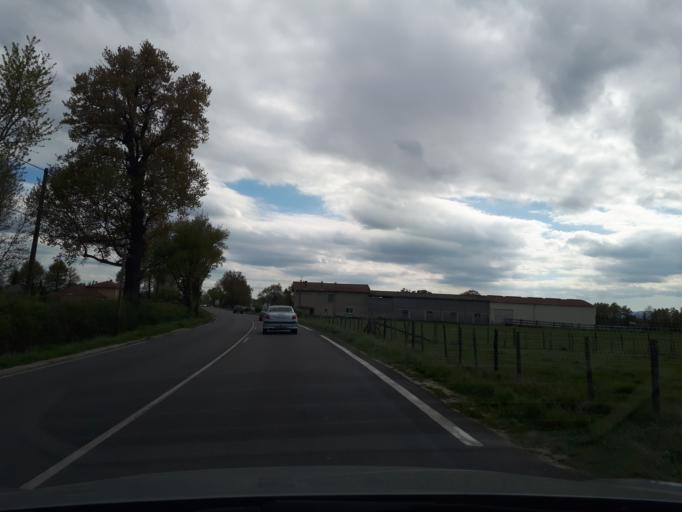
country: FR
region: Rhone-Alpes
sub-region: Departement de la Loire
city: Chamboeuf
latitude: 45.5795
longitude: 4.3046
